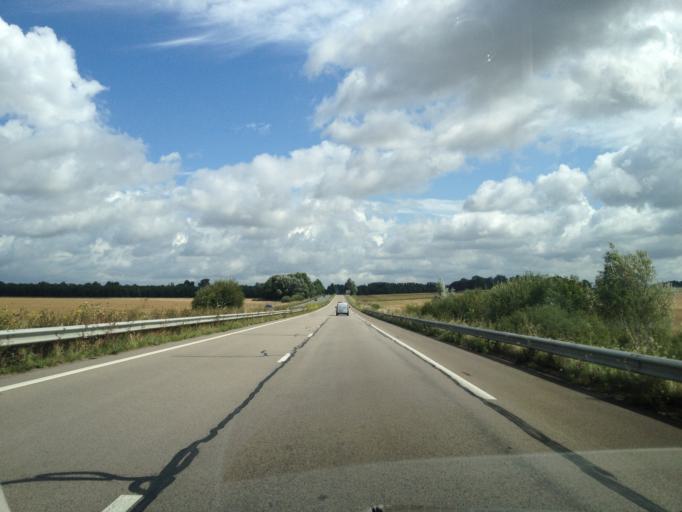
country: FR
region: Haute-Normandie
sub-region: Departement de la Seine-Maritime
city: Quincampoix
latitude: 49.5385
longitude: 1.2320
